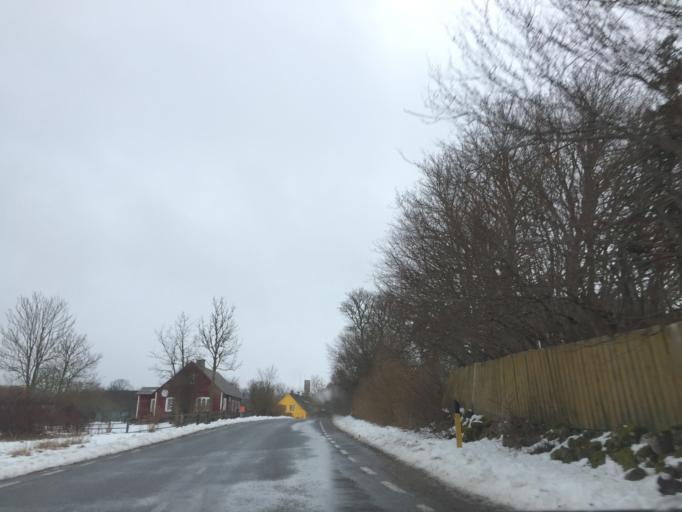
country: EE
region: Saare
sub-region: Kuressaare linn
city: Kuressaare
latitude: 58.3577
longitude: 22.0357
